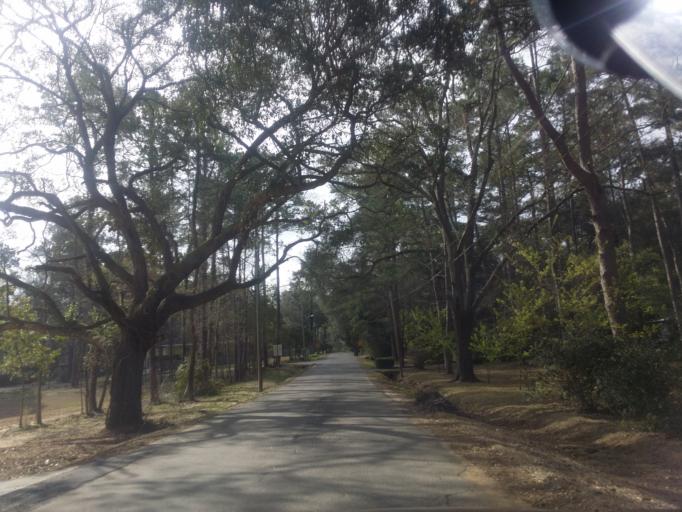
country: US
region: Florida
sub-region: Leon County
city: Tallahassee
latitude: 30.4481
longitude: -84.2401
